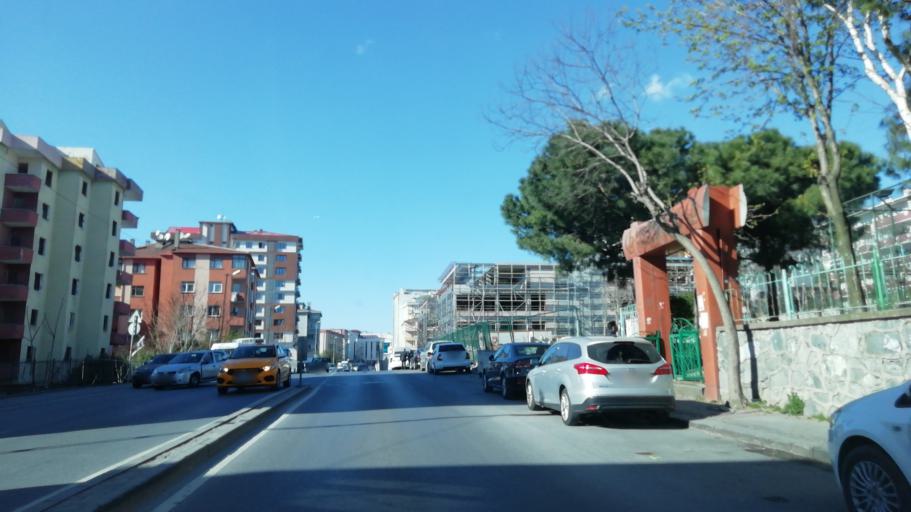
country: TR
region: Istanbul
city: Bagcilar
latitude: 41.0341
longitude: 28.8529
